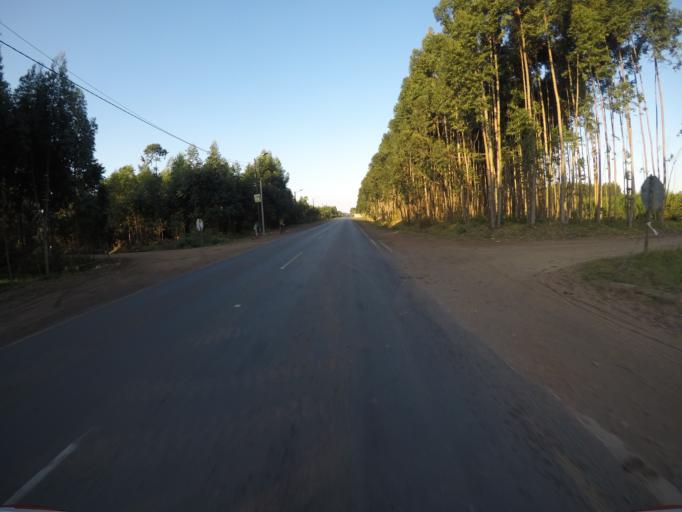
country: ZA
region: KwaZulu-Natal
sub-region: uThungulu District Municipality
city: KwaMbonambi
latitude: -28.6831
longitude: 32.1859
